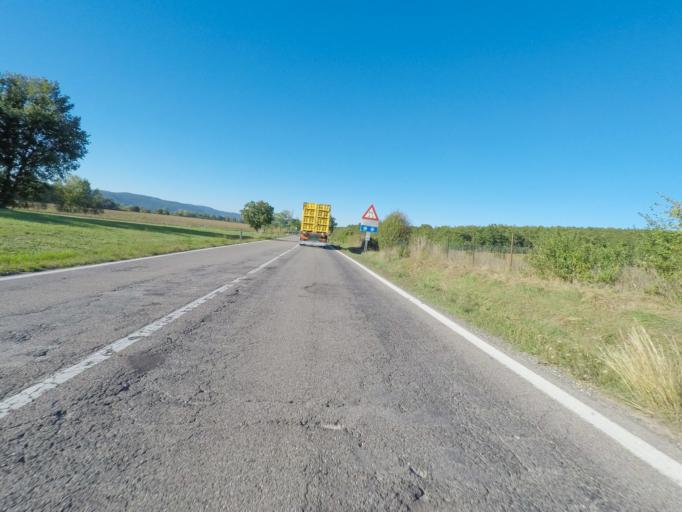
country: IT
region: Tuscany
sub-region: Provincia di Siena
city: Rosia
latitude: 43.2098
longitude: 11.2790
